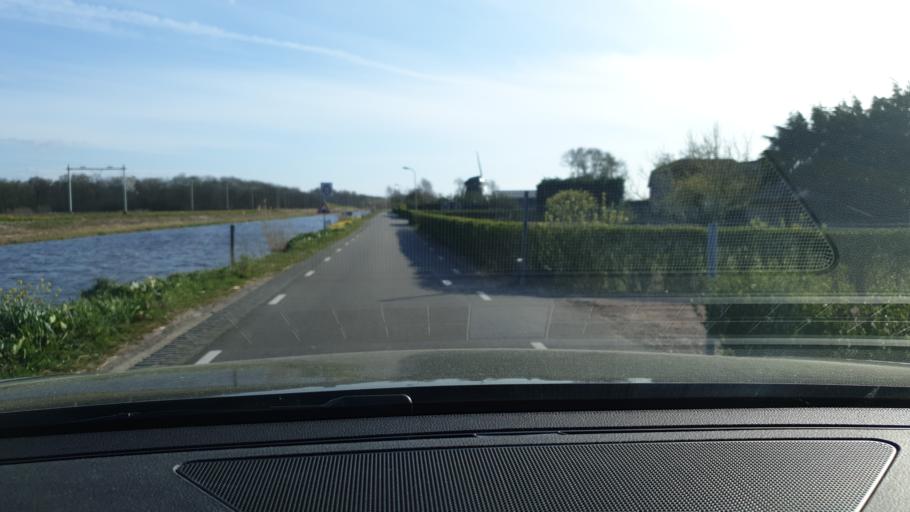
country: NL
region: South Holland
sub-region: Gemeente Lisse
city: Lisse
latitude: 52.2657
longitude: 4.5254
